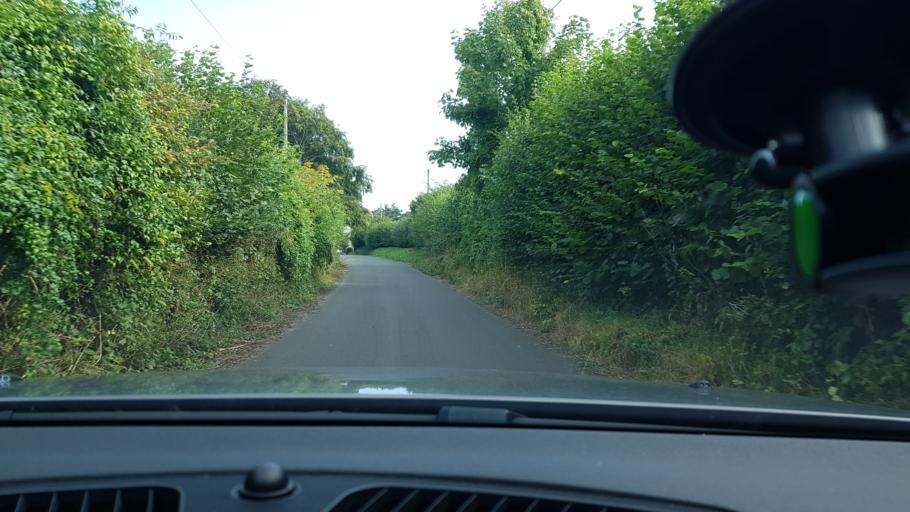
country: GB
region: England
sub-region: West Berkshire
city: Wickham
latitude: 51.4547
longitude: -1.4760
